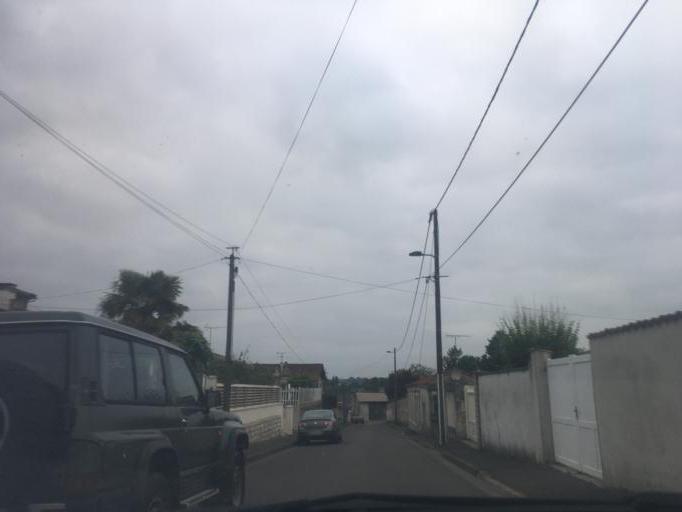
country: FR
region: Poitou-Charentes
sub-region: Departement de la Charente
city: Cognac
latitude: 45.6845
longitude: -0.3368
